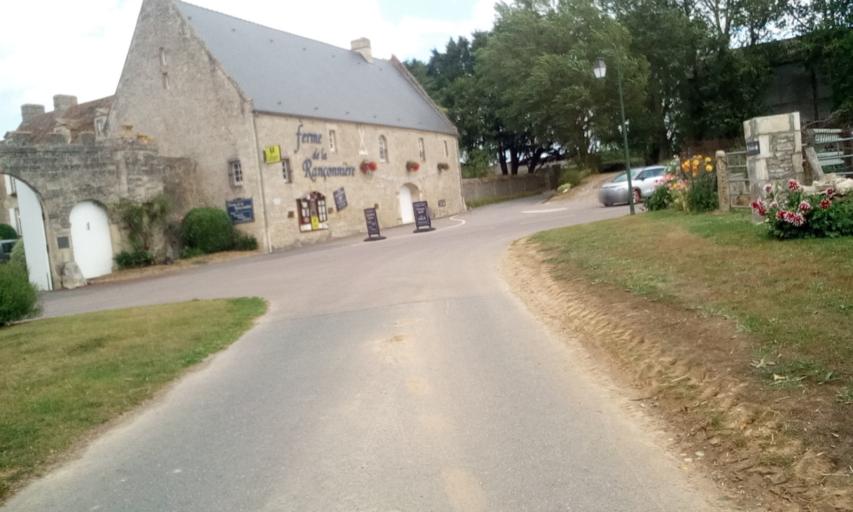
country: FR
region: Lower Normandy
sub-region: Departement du Calvados
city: Ver-sur-Mer
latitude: 49.3116
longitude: -0.5479
